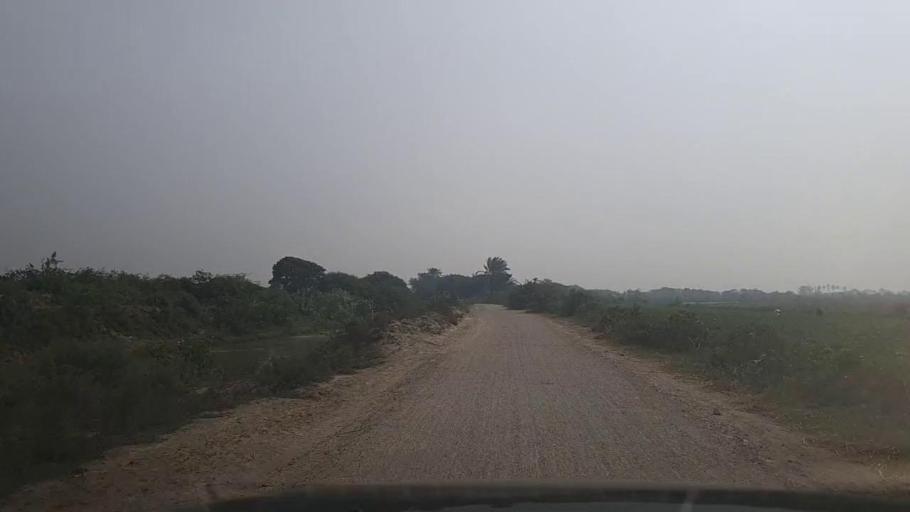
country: PK
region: Sindh
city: Mirpur Sakro
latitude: 24.4814
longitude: 67.6452
